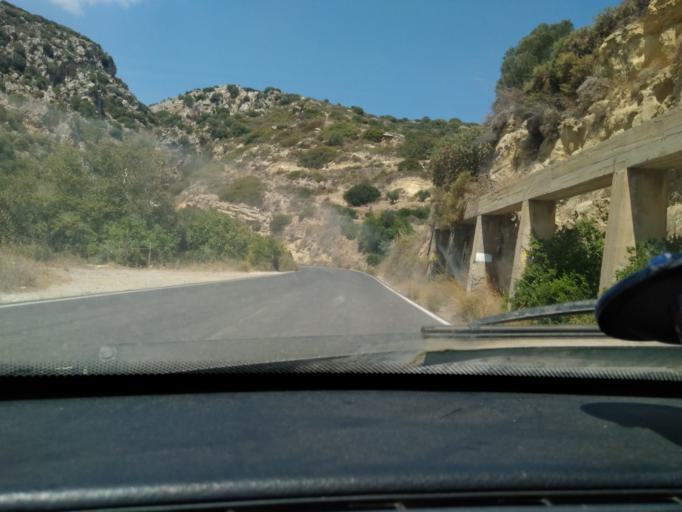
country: GR
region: Crete
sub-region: Nomos Lasithiou
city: Siteia
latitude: 35.1293
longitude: 26.0672
